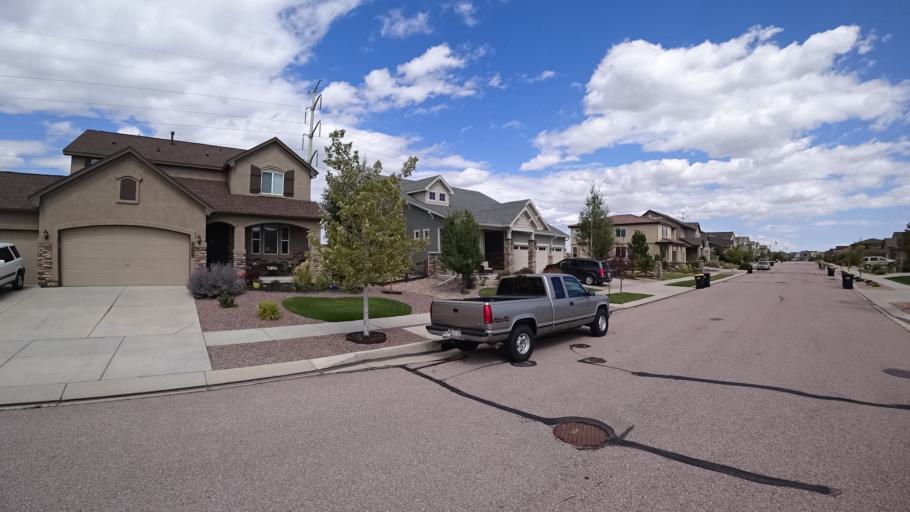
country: US
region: Colorado
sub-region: El Paso County
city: Black Forest
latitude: 38.9369
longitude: -104.6759
